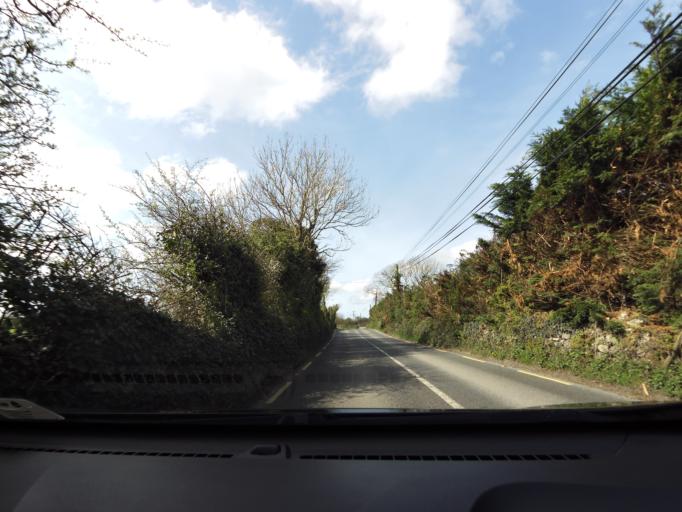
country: IE
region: Connaught
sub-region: County Galway
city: Athenry
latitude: 53.3062
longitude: -8.7749
